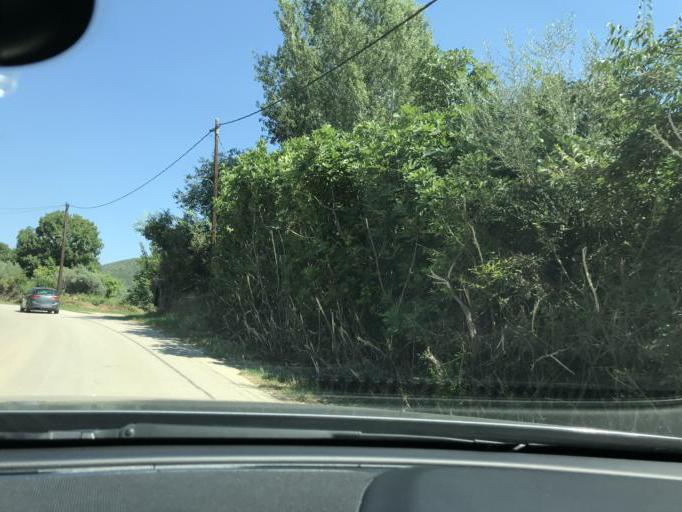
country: GR
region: Central Greece
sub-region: Nomos Fthiotidos
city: Kato Tithorea
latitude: 38.5179
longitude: 22.7483
